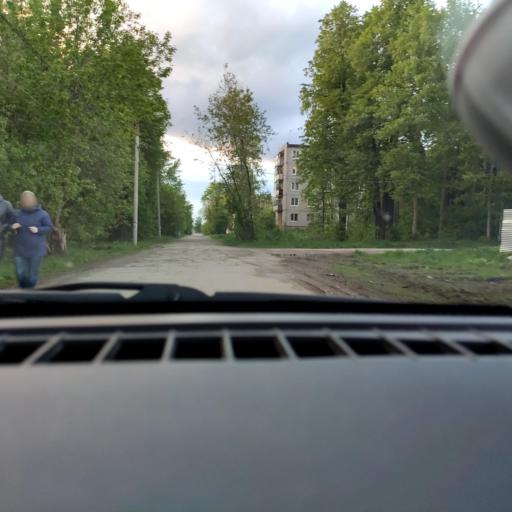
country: RU
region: Perm
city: Perm
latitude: 58.0850
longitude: 56.3858
